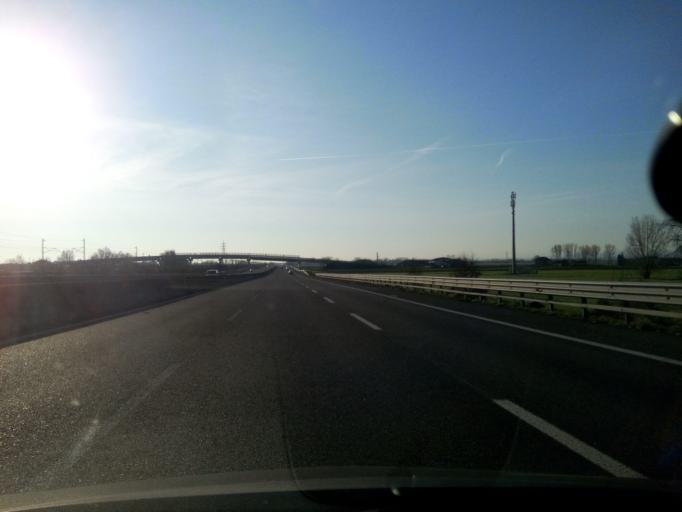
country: IT
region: Emilia-Romagna
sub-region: Provincia di Piacenza
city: Alseno
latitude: 44.9204
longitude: 9.9987
